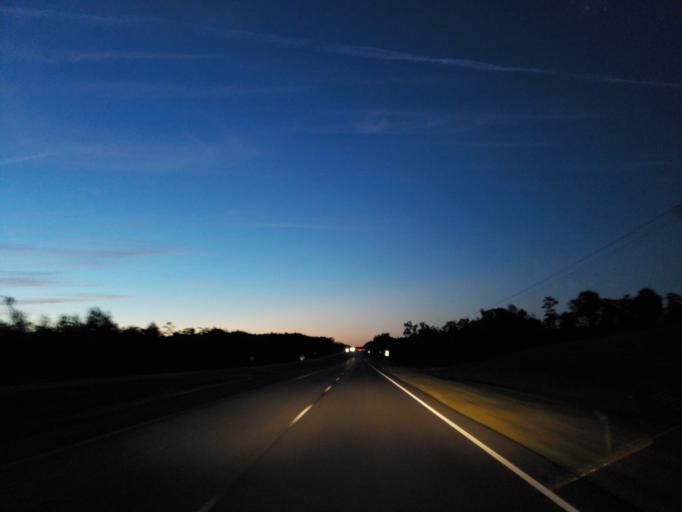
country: US
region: Mississippi
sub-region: Clarke County
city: Quitman
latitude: 32.0672
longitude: -88.6824
